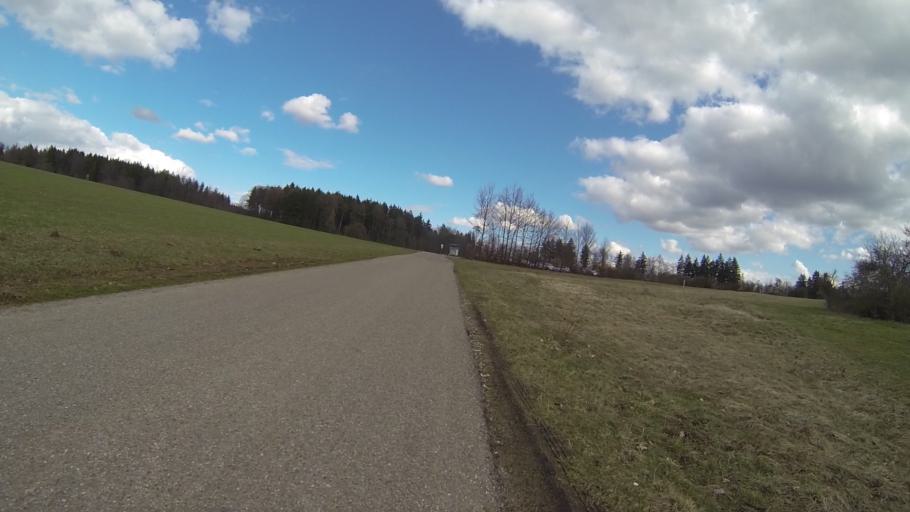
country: DE
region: Baden-Wuerttemberg
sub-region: Regierungsbezirk Stuttgart
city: Steinheim am Albuch
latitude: 48.6969
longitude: 10.1020
